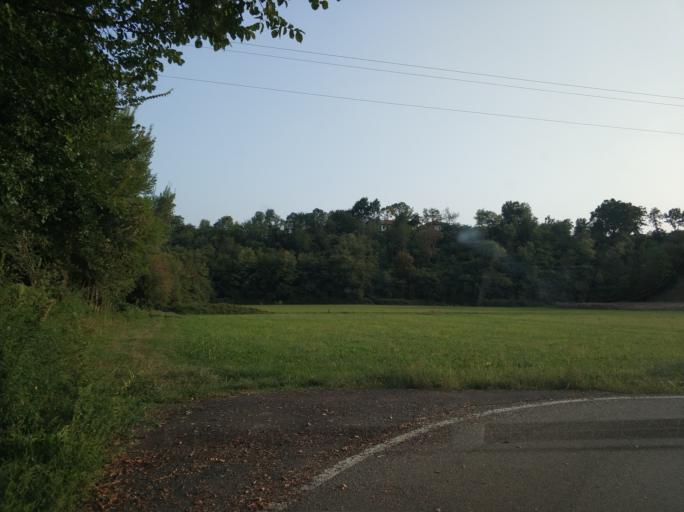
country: IT
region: Piedmont
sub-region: Provincia di Torino
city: Grosso
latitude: 45.2609
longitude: 7.5579
